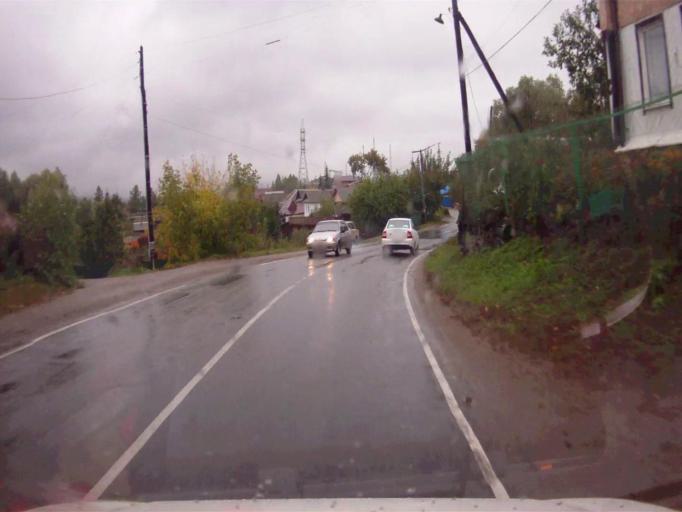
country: RU
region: Chelyabinsk
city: Kyshtym
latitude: 55.7242
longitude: 60.5250
